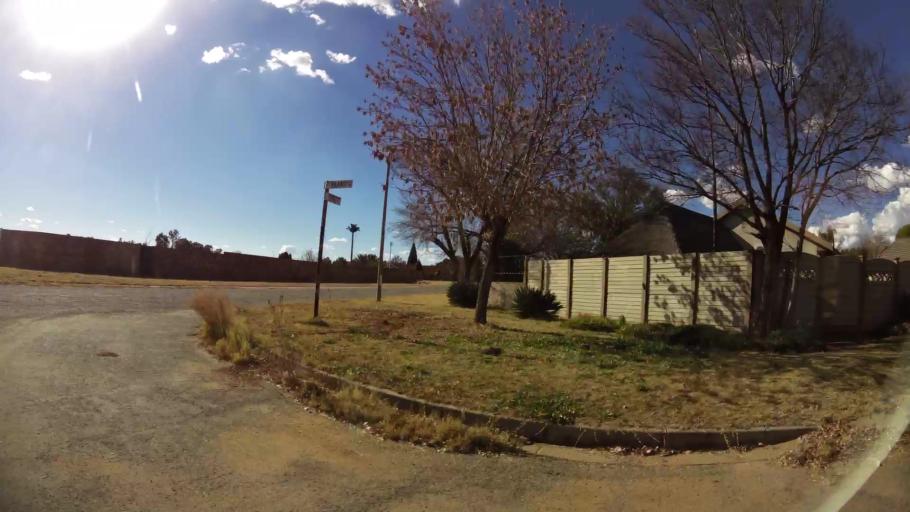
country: ZA
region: North-West
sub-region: Dr Kenneth Kaunda District Municipality
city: Klerksdorp
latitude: -26.8414
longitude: 26.6491
